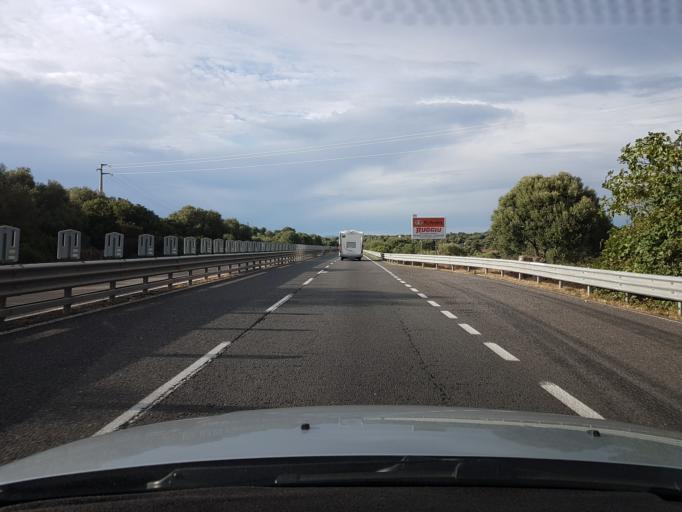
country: IT
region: Sardinia
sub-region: Provincia di Oristano
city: Paulilatino
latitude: 40.0801
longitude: 8.7519
